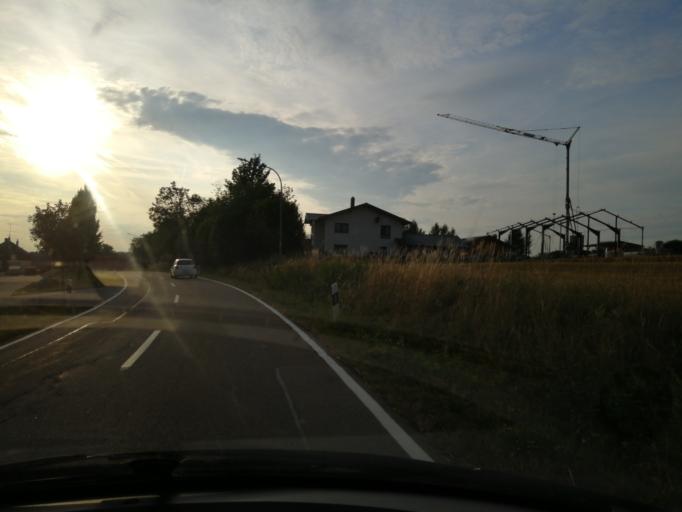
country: DE
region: Bavaria
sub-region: Lower Bavaria
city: Wiesenfelden
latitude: 49.0565
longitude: 12.5818
